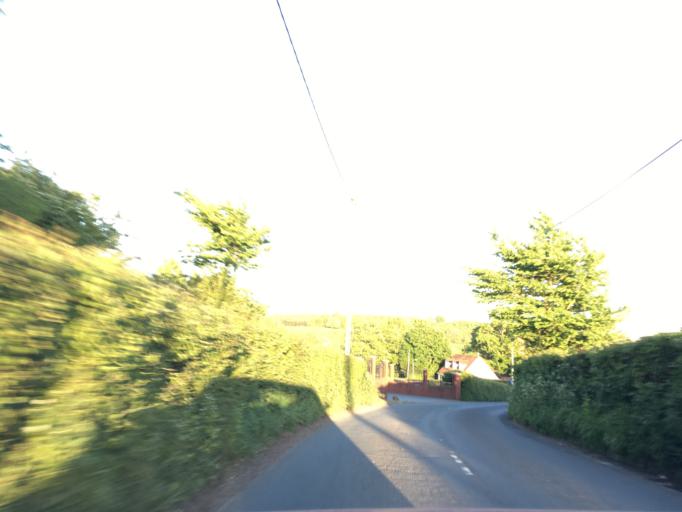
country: GB
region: Wales
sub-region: Newport
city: Llanwern
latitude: 51.5915
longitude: -2.9164
